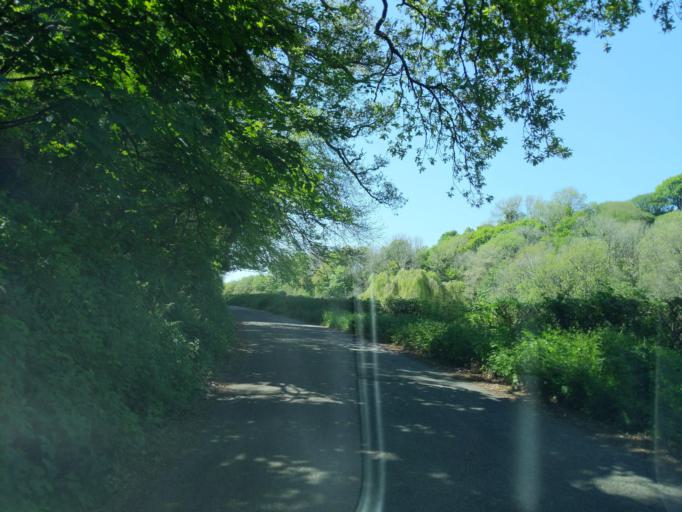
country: GB
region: England
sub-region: Cornwall
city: Pillaton
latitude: 50.4126
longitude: -4.3296
